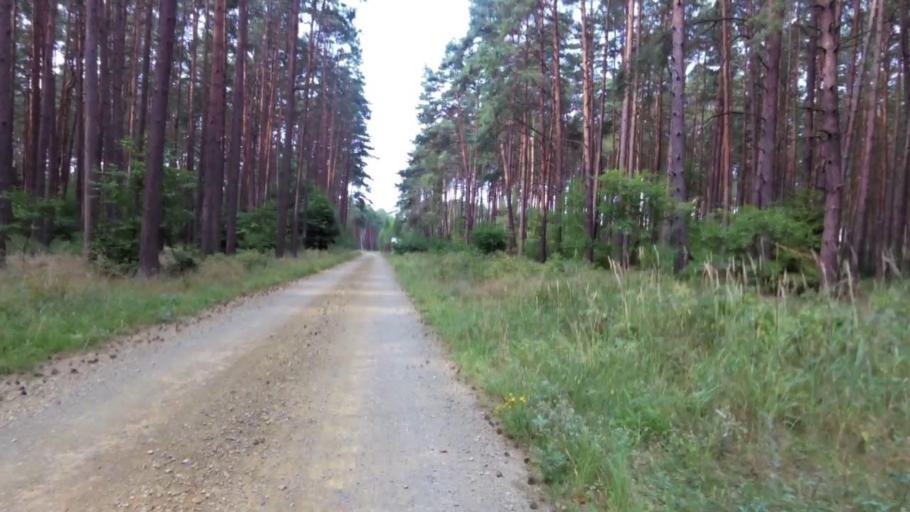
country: PL
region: West Pomeranian Voivodeship
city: Trzcinsko Zdroj
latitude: 52.8490
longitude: 14.6185
